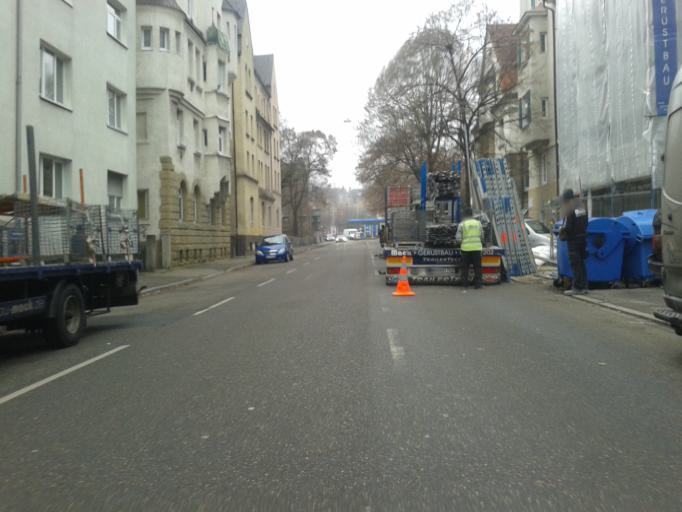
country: DE
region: Baden-Wuerttemberg
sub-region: Tuebingen Region
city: Ulm
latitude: 48.4065
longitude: 9.9990
